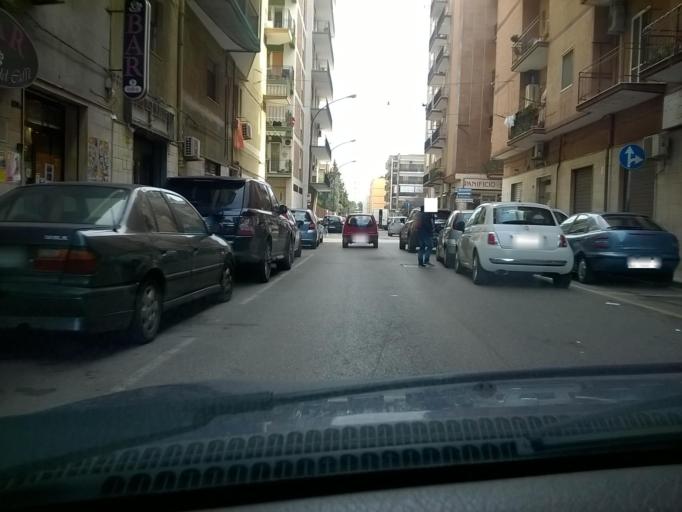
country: IT
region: Apulia
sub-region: Provincia di Taranto
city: Taranto
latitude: 40.4671
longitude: 17.2615
